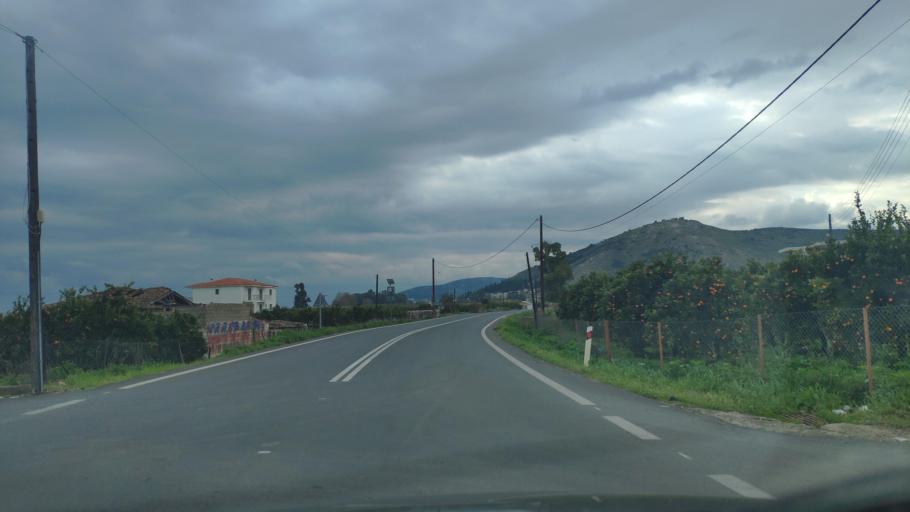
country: GR
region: Peloponnese
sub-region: Nomos Argolidos
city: Nea Kios
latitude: 37.5686
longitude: 22.7103
